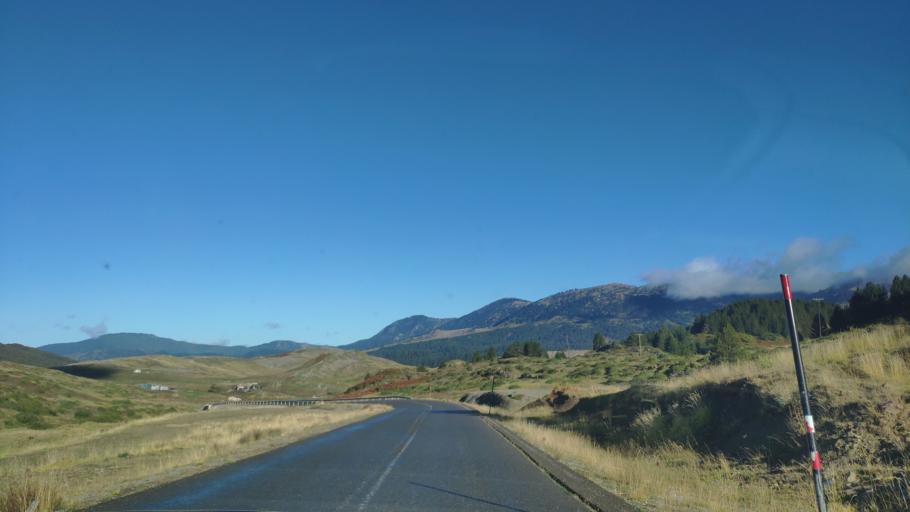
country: GR
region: Epirus
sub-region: Nomos Ioanninon
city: Metsovo
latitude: 39.8035
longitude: 21.1736
